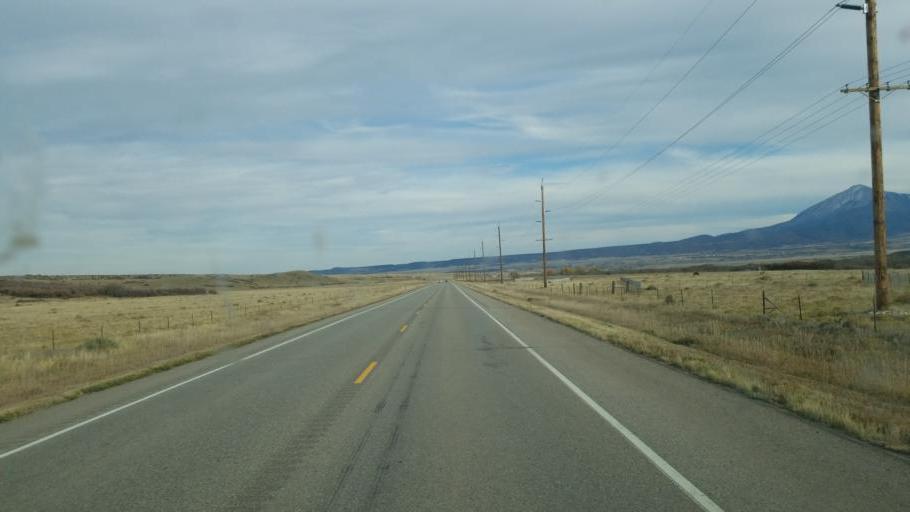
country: US
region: Colorado
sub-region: Huerfano County
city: Walsenburg
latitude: 37.5454
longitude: -105.0845
